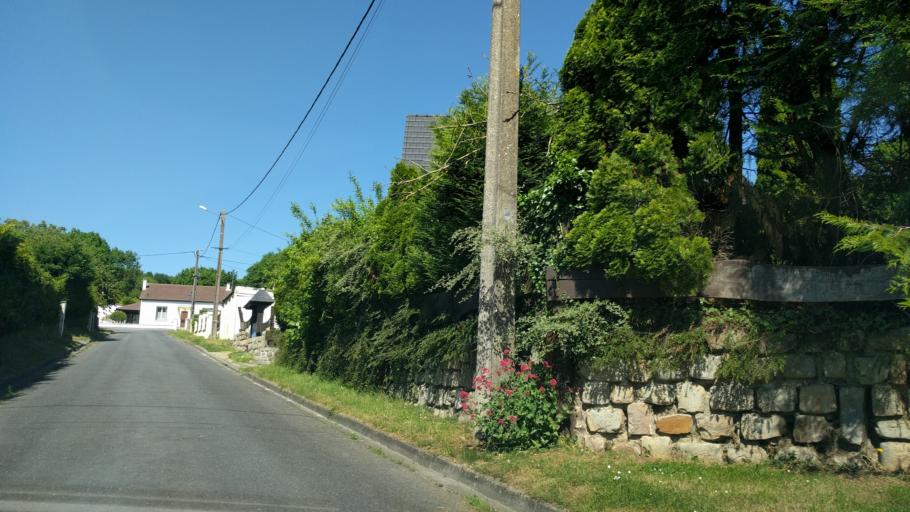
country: FR
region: Picardie
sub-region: Departement de la Somme
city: Peronne
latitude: 49.9455
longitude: 2.9357
